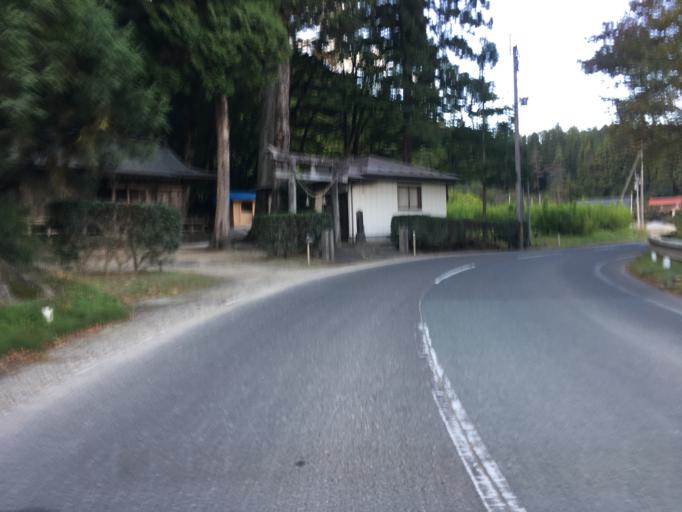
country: JP
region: Miyagi
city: Marumori
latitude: 37.8352
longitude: 140.8332
